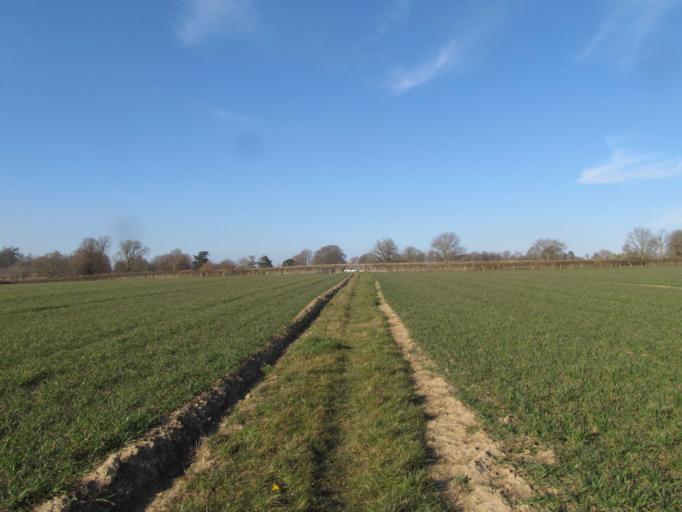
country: GB
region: England
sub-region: West Sussex
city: Petworth
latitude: 50.9831
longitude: -0.6172
